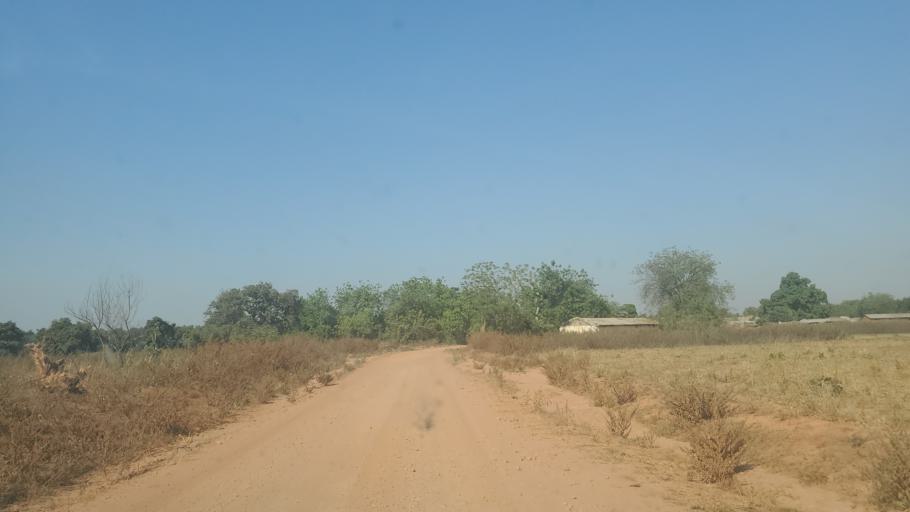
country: NG
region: Niger
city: Badeggi
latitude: 9.1251
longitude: 6.1935
